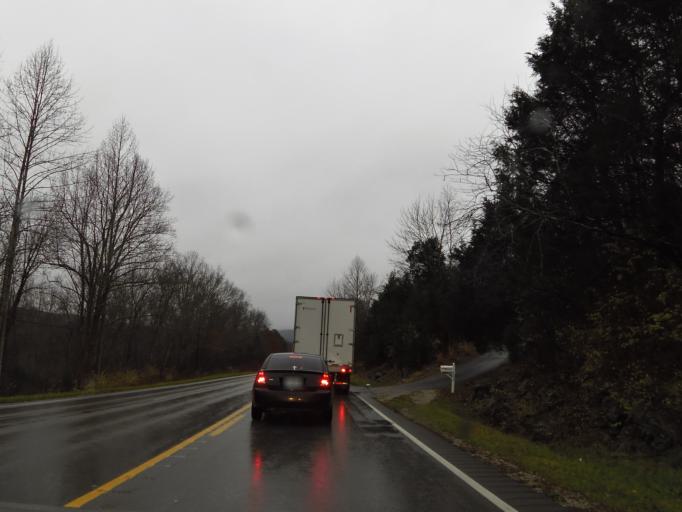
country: US
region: Kentucky
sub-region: Rockcastle County
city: Mount Vernon
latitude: 37.4056
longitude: -84.3358
